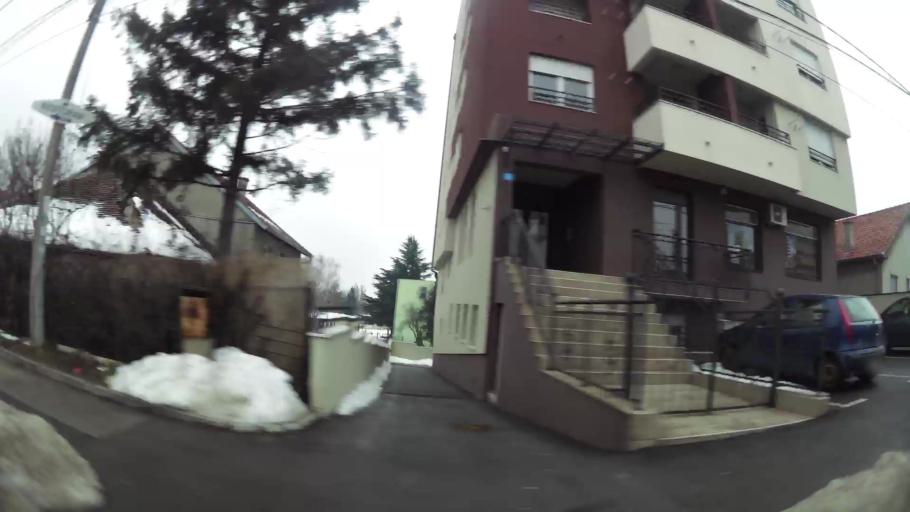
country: RS
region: Central Serbia
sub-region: Belgrade
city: Vozdovac
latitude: 44.7510
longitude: 20.4935
